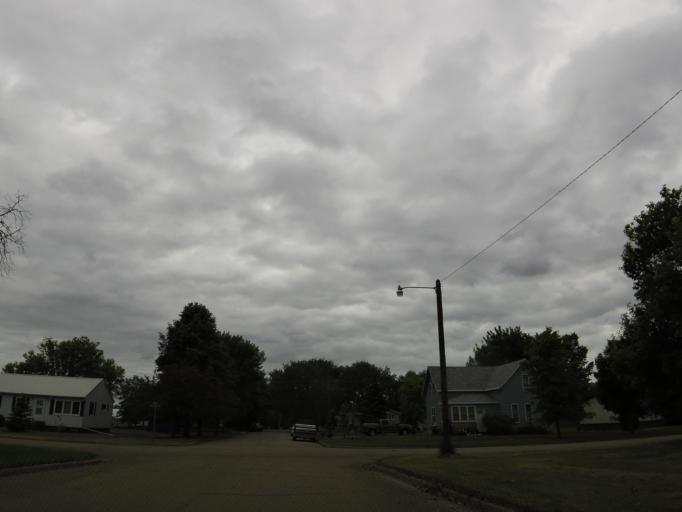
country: US
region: North Dakota
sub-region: Walsh County
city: Grafton
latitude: 48.6171
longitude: -97.4503
